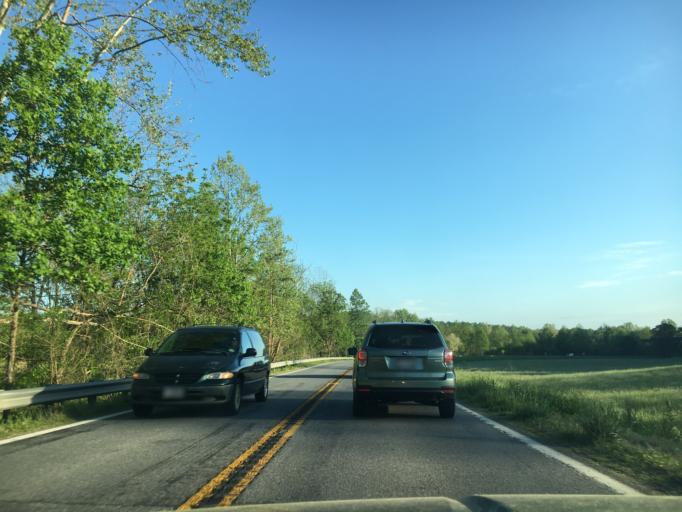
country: US
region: Virginia
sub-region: Campbell County
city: Rustburg
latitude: 37.2984
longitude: -79.1108
